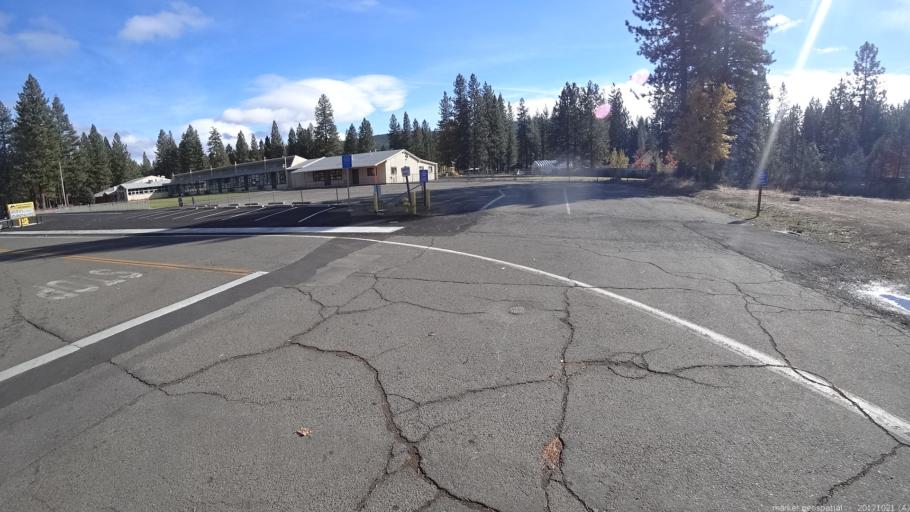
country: US
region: California
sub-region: Shasta County
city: Burney
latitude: 40.8833
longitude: -121.6566
